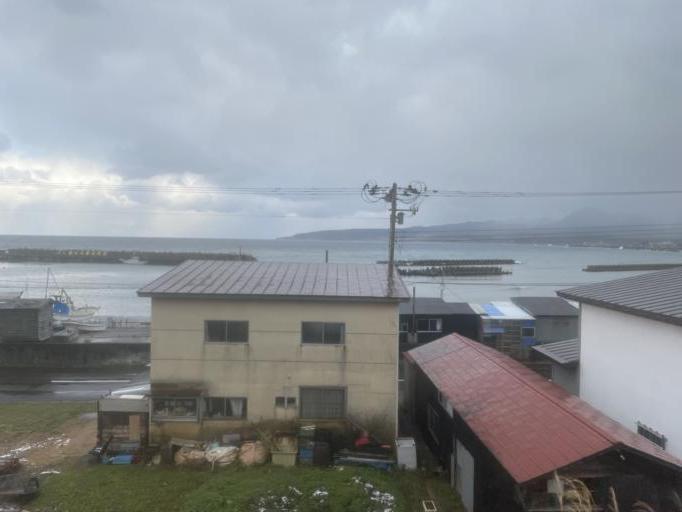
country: JP
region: Aomori
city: Shimokizukuri
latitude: 41.1835
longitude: 140.4606
